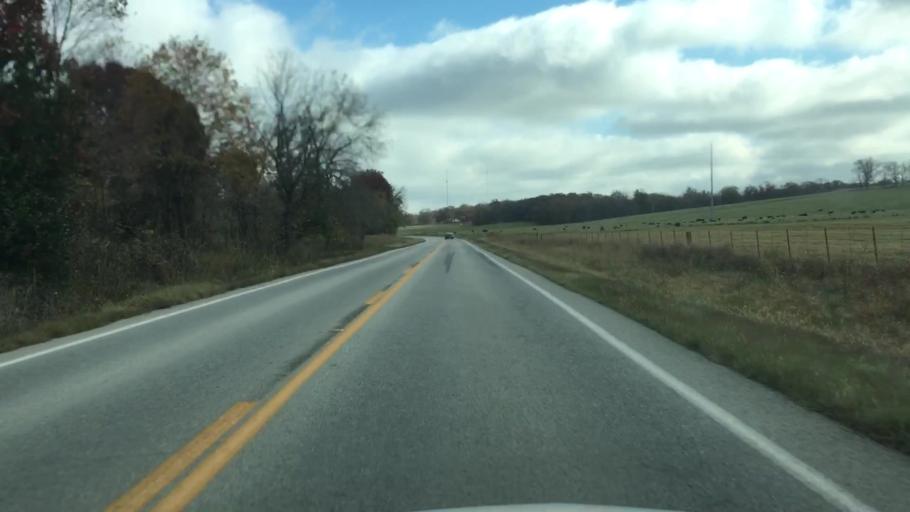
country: US
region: Arkansas
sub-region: Benton County
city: Gentry
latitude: 36.2582
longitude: -94.4068
